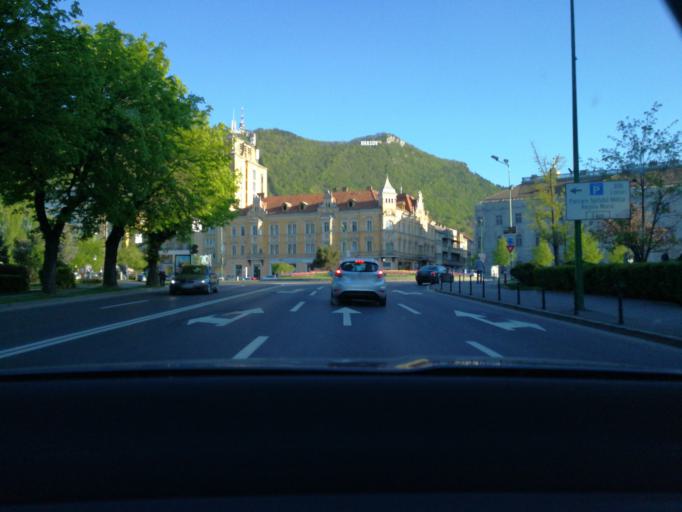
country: RO
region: Brasov
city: Brasov
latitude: 45.6463
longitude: 25.5895
